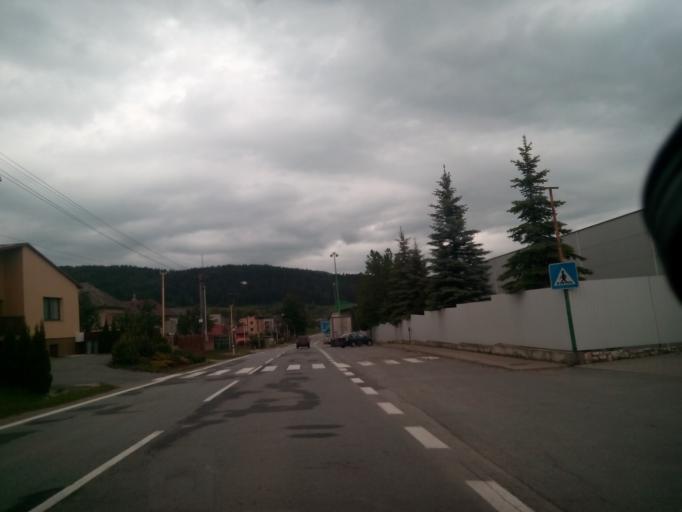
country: SK
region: Kosicky
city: Krompachy
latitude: 49.0046
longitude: 20.9424
